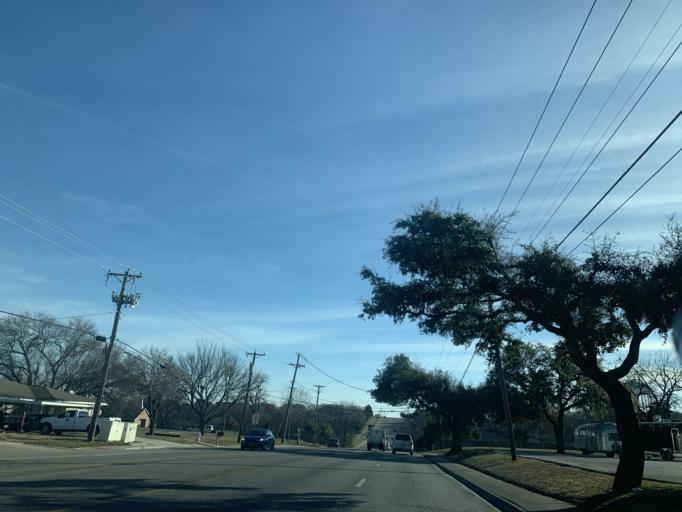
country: US
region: Texas
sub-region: Dallas County
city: DeSoto
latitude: 32.5897
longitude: -96.8514
